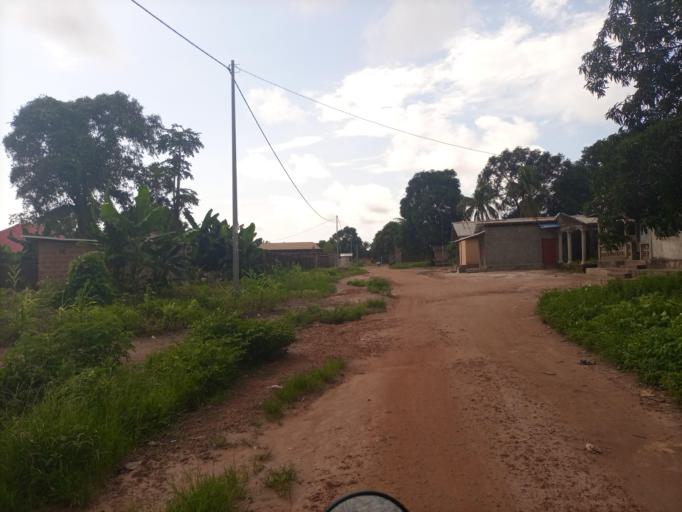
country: SL
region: Northern Province
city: Masoyila
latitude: 8.6002
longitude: -13.1746
